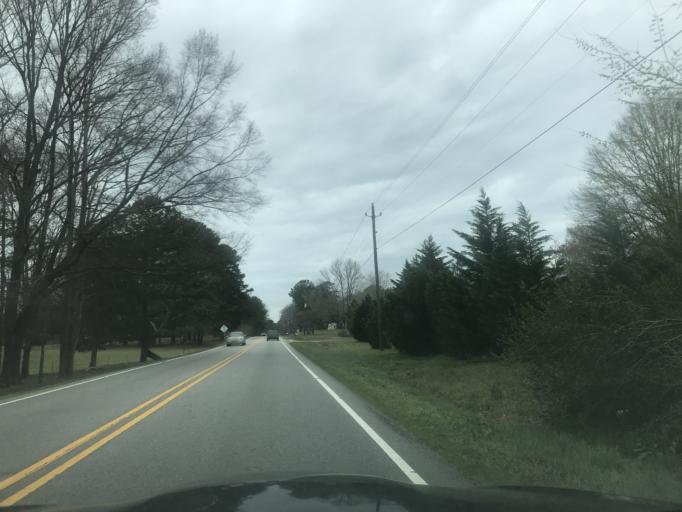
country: US
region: North Carolina
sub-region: Franklin County
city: Franklinton
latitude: 36.1089
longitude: -78.4747
